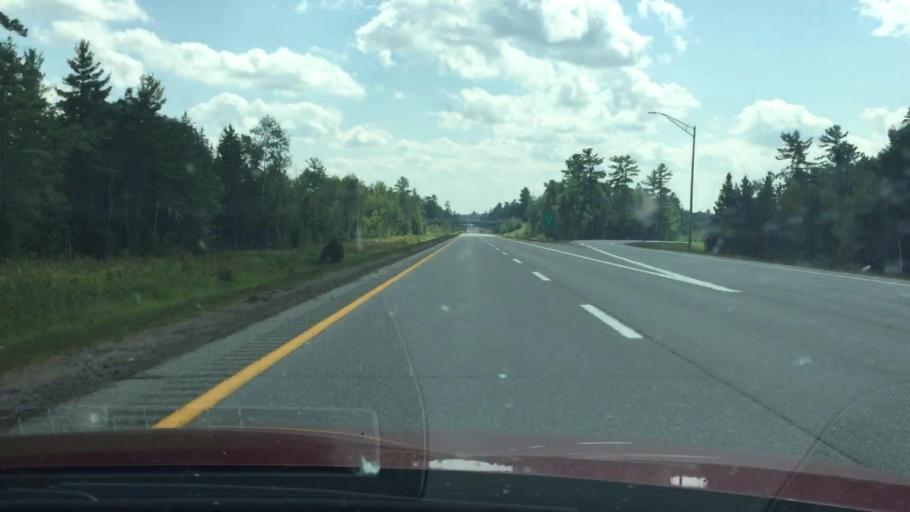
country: US
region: Maine
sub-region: Penobscot County
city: Lincoln
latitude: 45.3805
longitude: -68.6055
